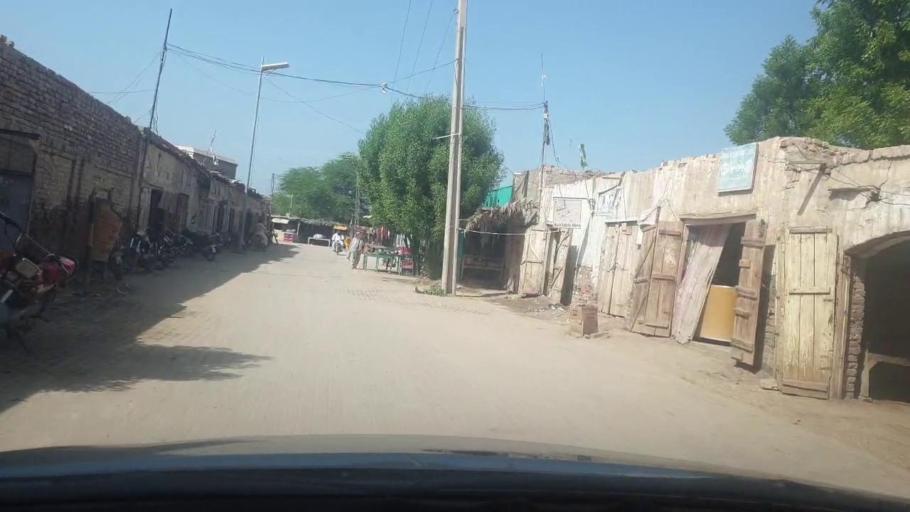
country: PK
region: Sindh
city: Gambat
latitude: 27.3373
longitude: 68.5455
